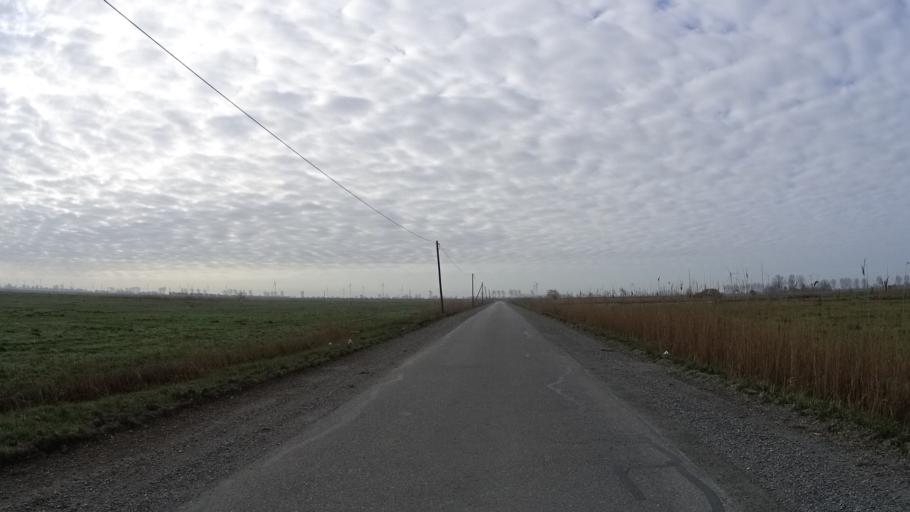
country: DE
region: Lower Saxony
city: Emden
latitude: 53.4057
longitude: 7.3060
